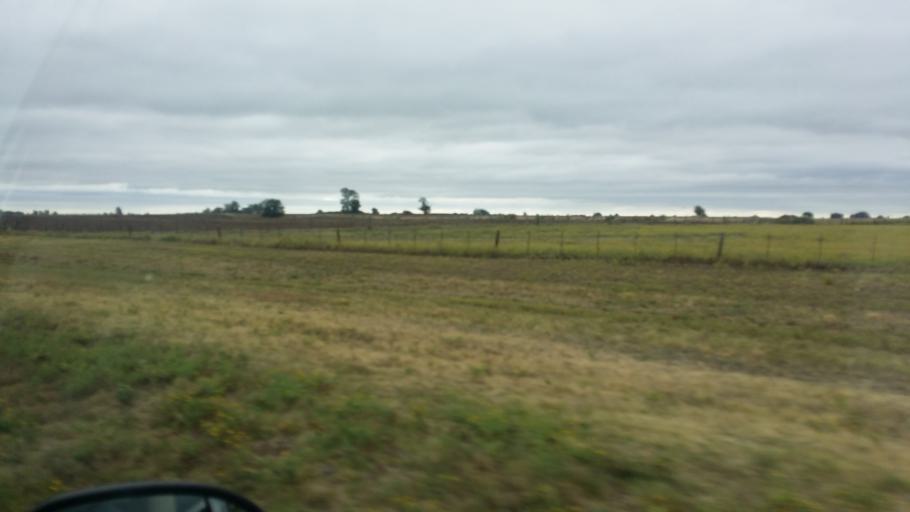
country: AR
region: La Pampa
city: Uriburu
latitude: -36.5164
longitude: -63.7464
